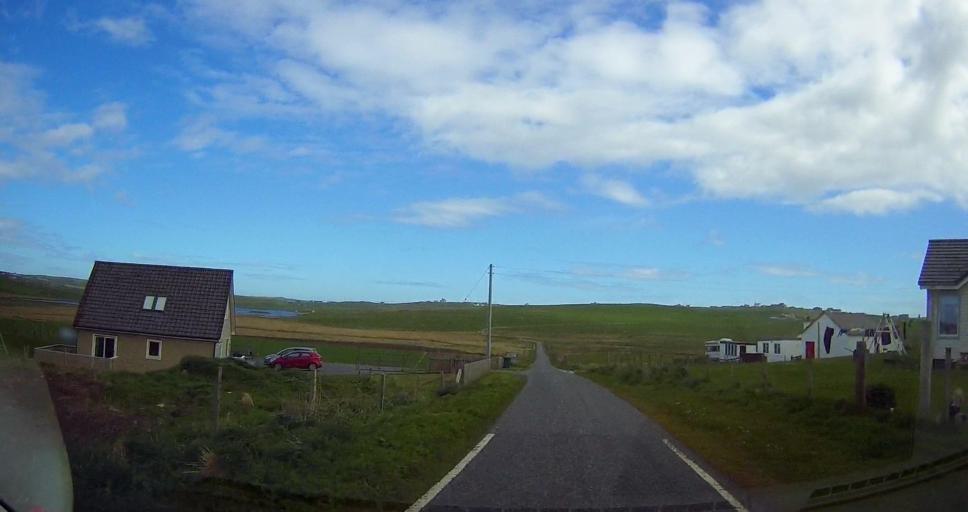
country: GB
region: Scotland
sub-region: Shetland Islands
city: Sandwick
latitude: 59.9232
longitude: -1.3301
